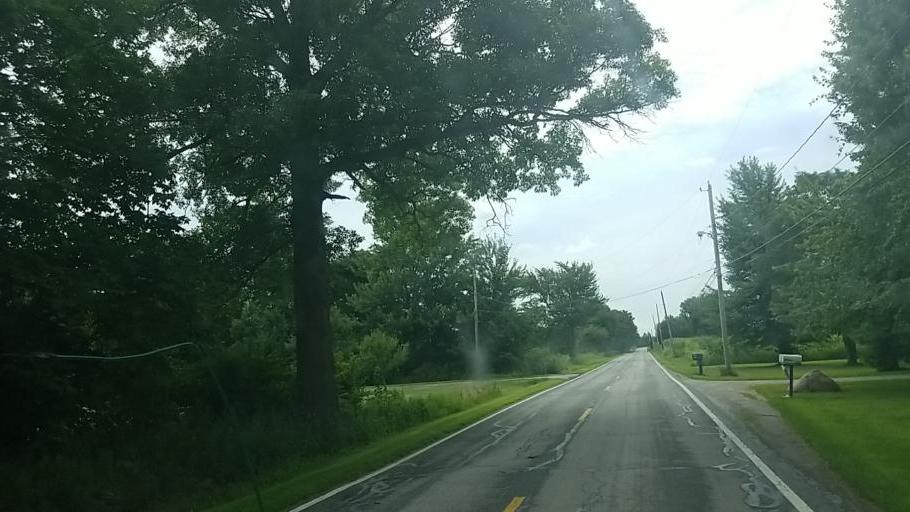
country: US
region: Ohio
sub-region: Franklin County
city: New Albany
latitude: 40.1413
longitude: -82.8227
